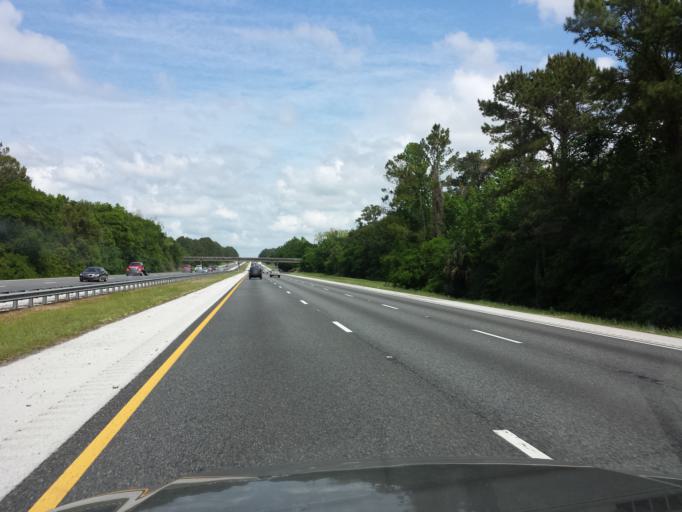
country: US
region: Florida
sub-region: Marion County
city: Citra
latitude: 29.3639
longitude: -82.2250
